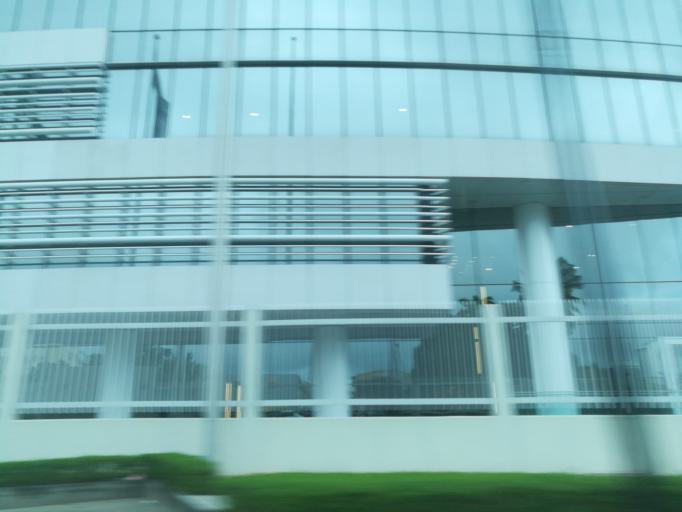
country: NG
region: Lagos
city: Ikoyi
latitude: 6.4267
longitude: 3.4239
